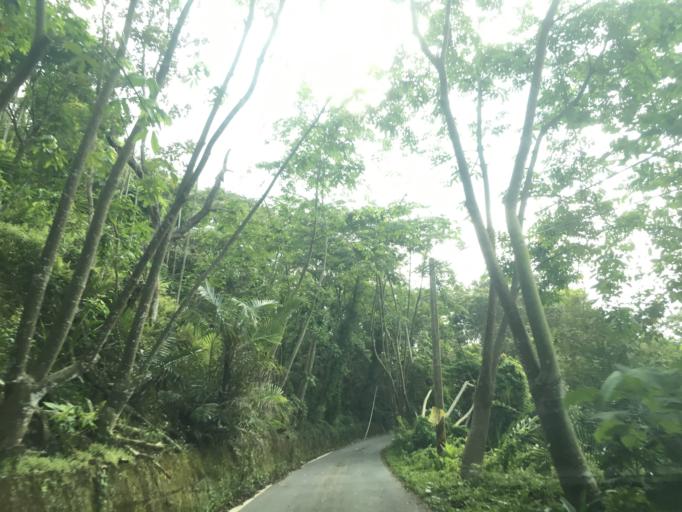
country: TW
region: Taiwan
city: Zhongxing New Village
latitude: 23.9699
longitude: 120.8175
